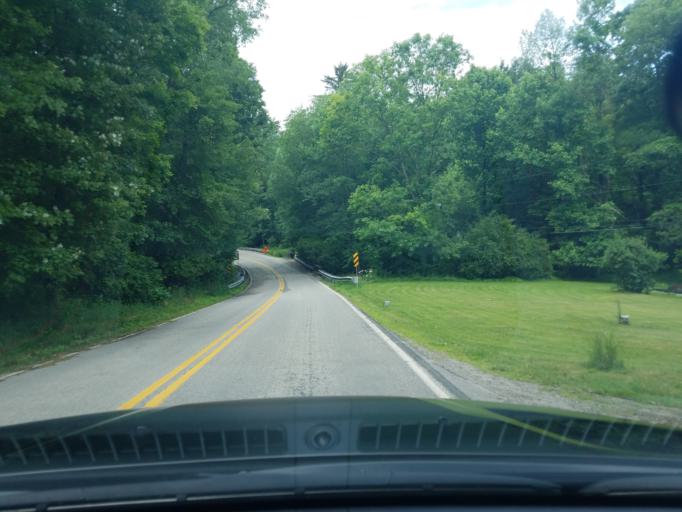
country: US
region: Pennsylvania
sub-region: Fayette County
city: Bear Rocks
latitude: 40.1790
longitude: -79.3685
